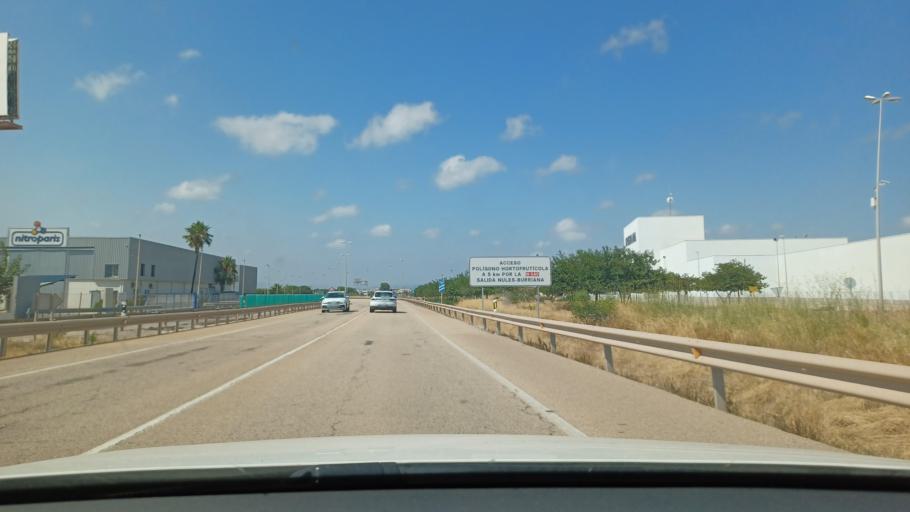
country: ES
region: Valencia
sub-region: Provincia de Castello
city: Nules
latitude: 39.8299
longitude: -0.1647
